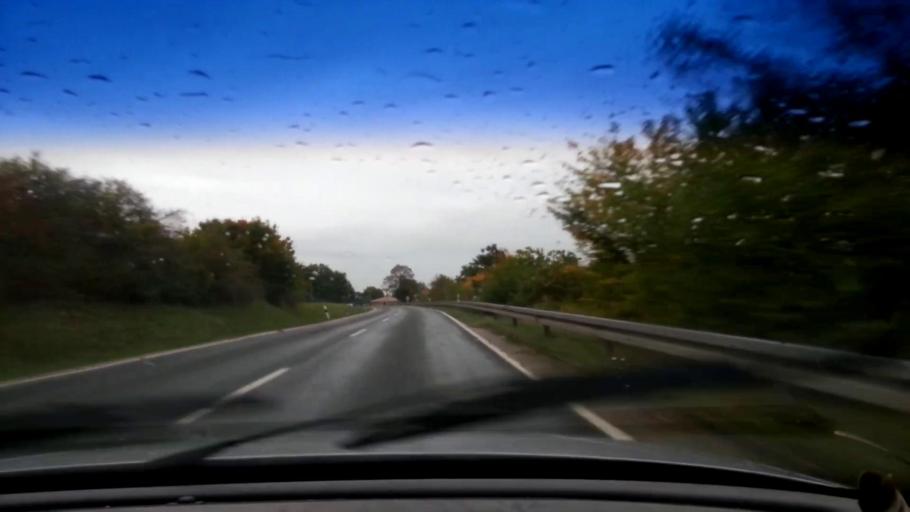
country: DE
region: Bavaria
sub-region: Upper Franconia
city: Priesendorf
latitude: 49.8602
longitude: 10.6823
